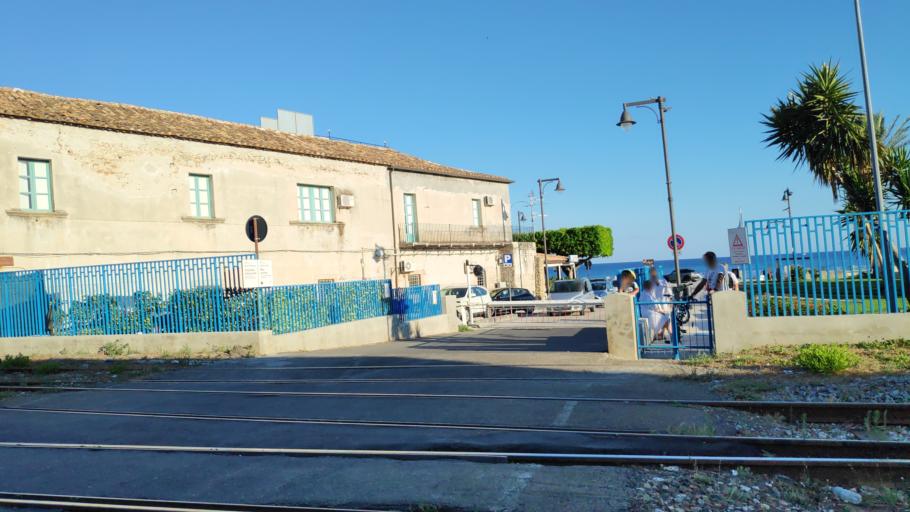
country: IT
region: Calabria
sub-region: Provincia di Reggio Calabria
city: Roccella Ionica
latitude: 38.3216
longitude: 16.4050
